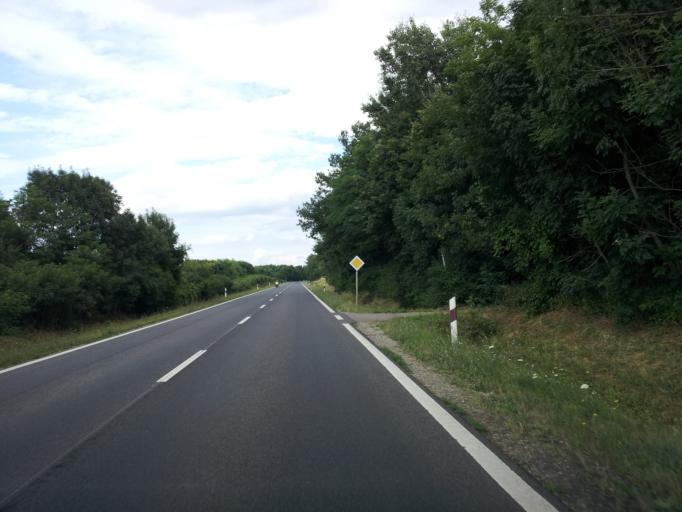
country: HU
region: Vas
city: Janoshaza
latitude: 47.1093
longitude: 17.0970
